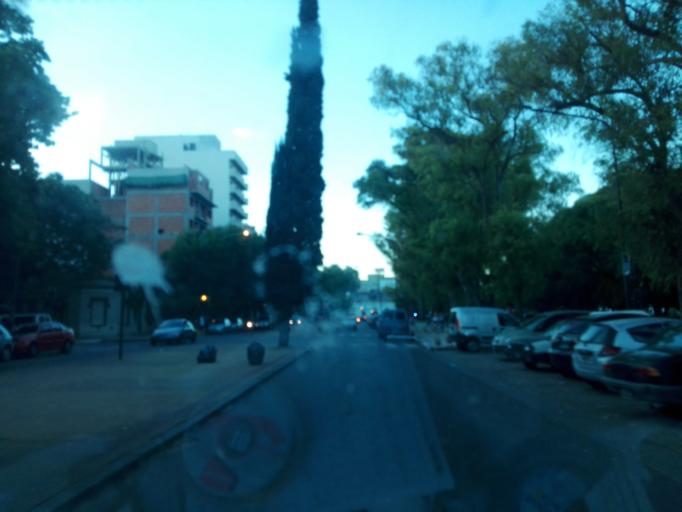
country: AR
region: Buenos Aires
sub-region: Partido de La Plata
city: La Plata
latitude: -34.9318
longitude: -57.9427
